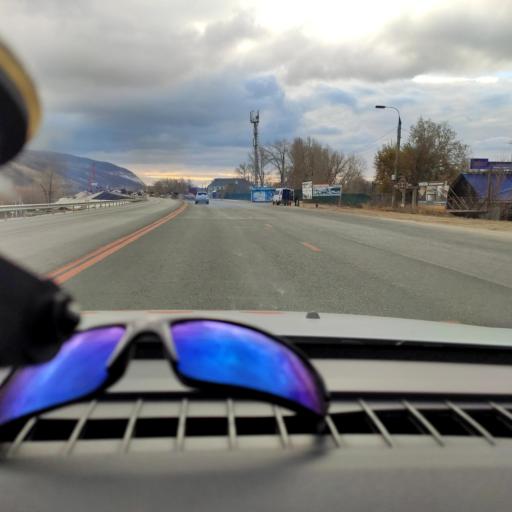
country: RU
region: Samara
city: Volzhskiy
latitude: 53.4178
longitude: 50.1286
